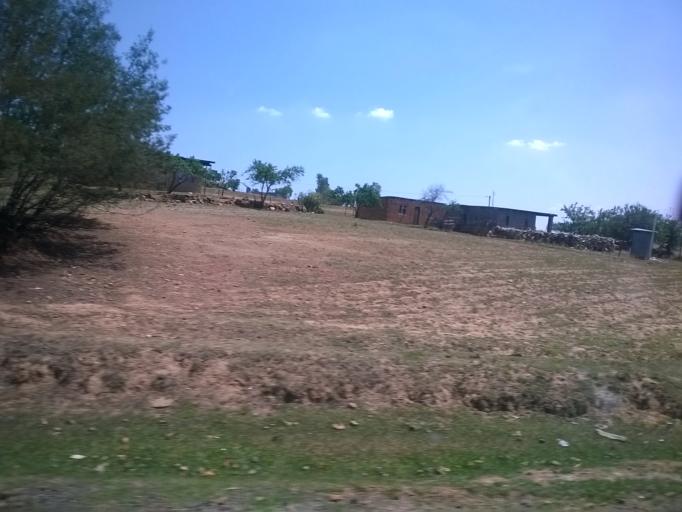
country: LS
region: Berea
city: Teyateyaneng
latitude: -29.1037
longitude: 27.8373
